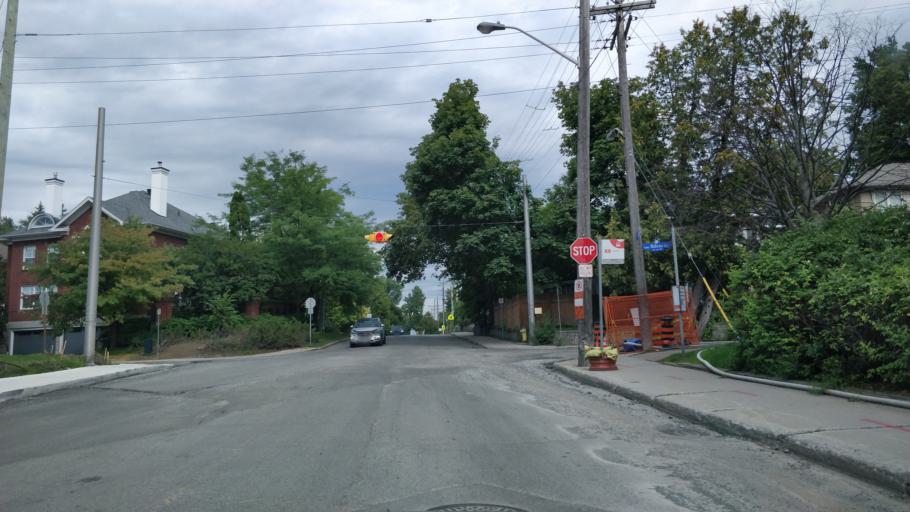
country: CA
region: Ontario
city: Ottawa
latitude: 45.4434
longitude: -75.6772
